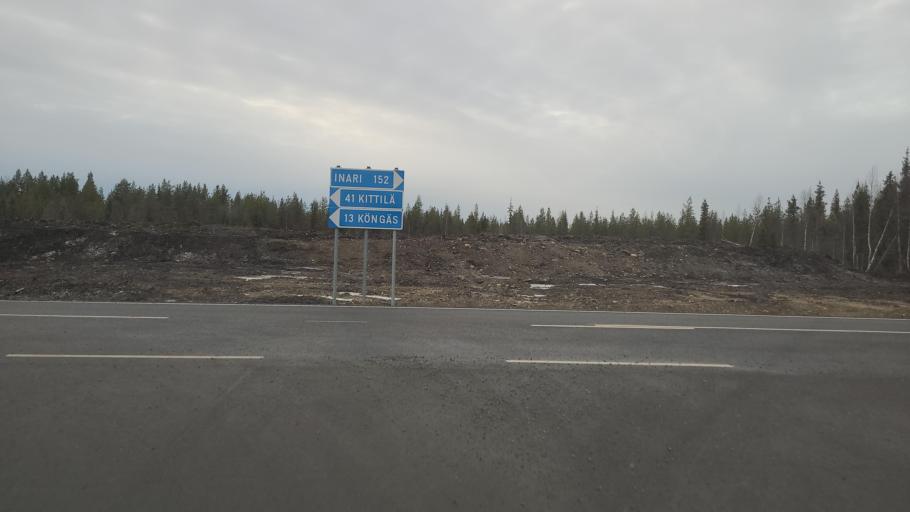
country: FI
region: Lapland
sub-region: Tunturi-Lappi
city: Kittilae
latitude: 67.9040
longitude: 25.0791
